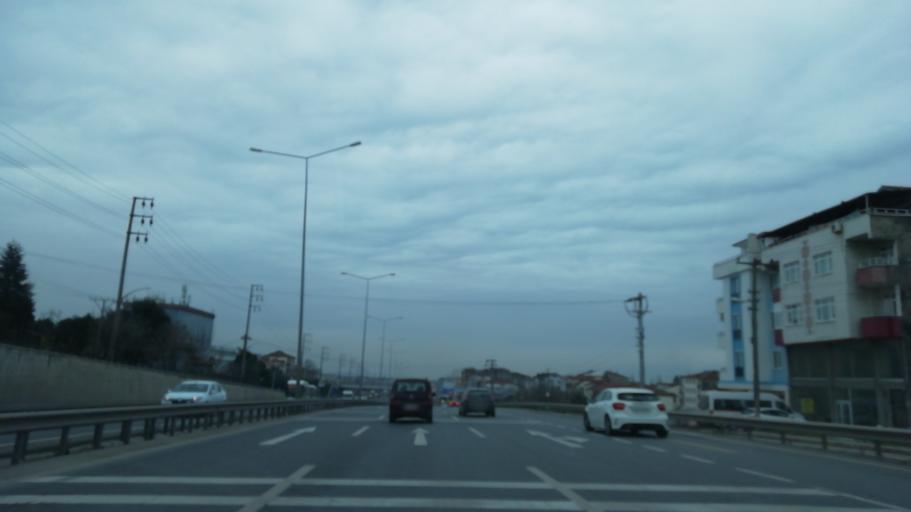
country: TR
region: Kocaeli
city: Derince
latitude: 40.7566
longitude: 29.8125
